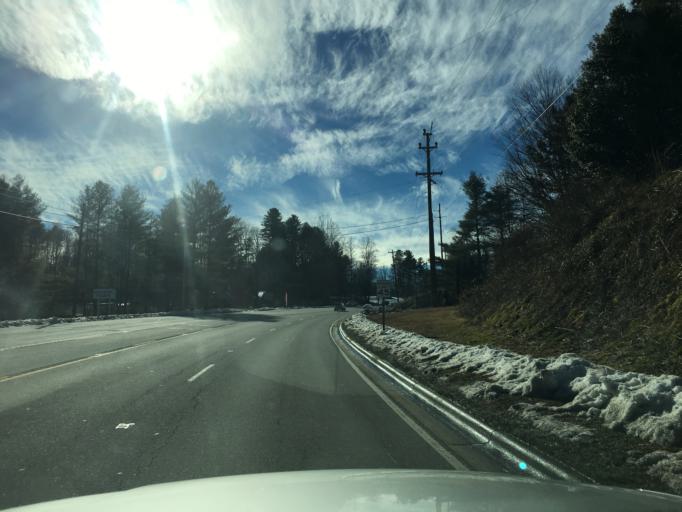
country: US
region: North Carolina
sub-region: Transylvania County
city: Brevard
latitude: 35.2180
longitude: -82.7507
